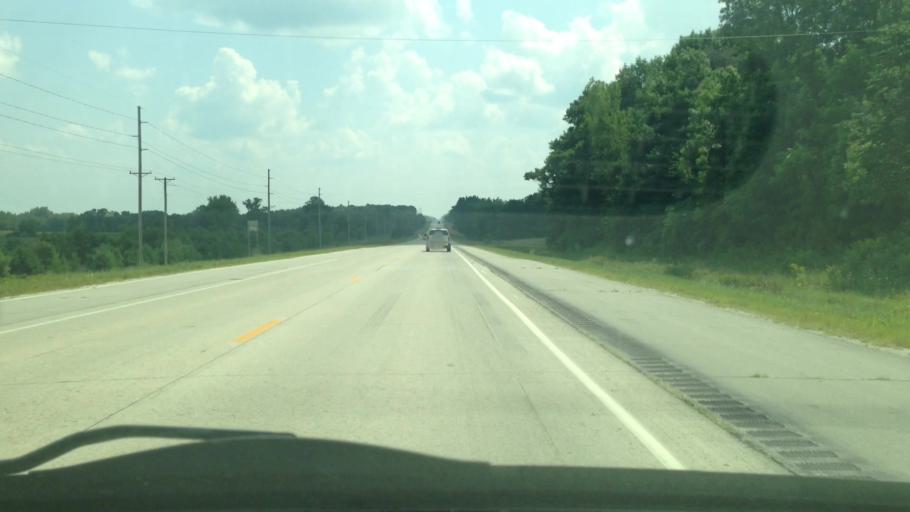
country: US
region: Minnesota
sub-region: Fillmore County
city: Spring Valley
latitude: 43.6307
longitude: -92.3902
